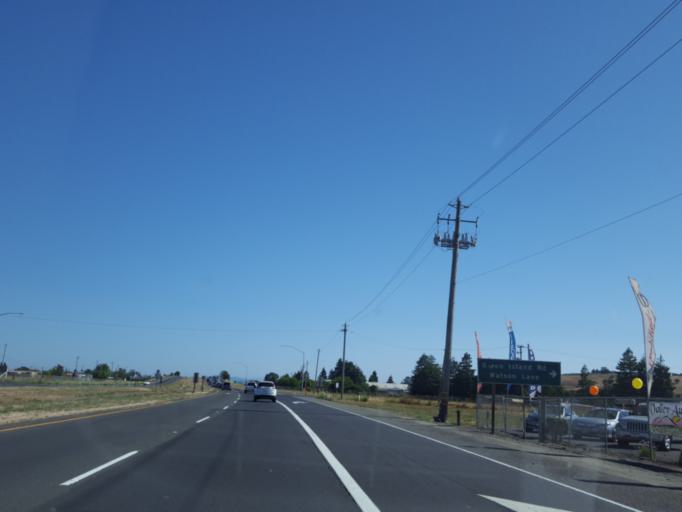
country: US
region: California
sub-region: Napa County
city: American Canyon
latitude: 38.1972
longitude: -122.2563
